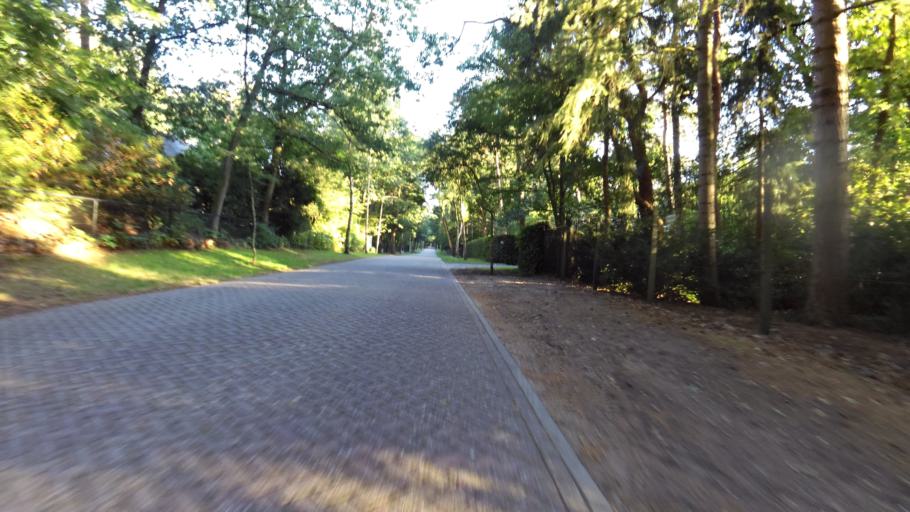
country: NL
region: Utrecht
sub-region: Gemeente Zeist
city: Zeist
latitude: 52.1276
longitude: 5.2449
